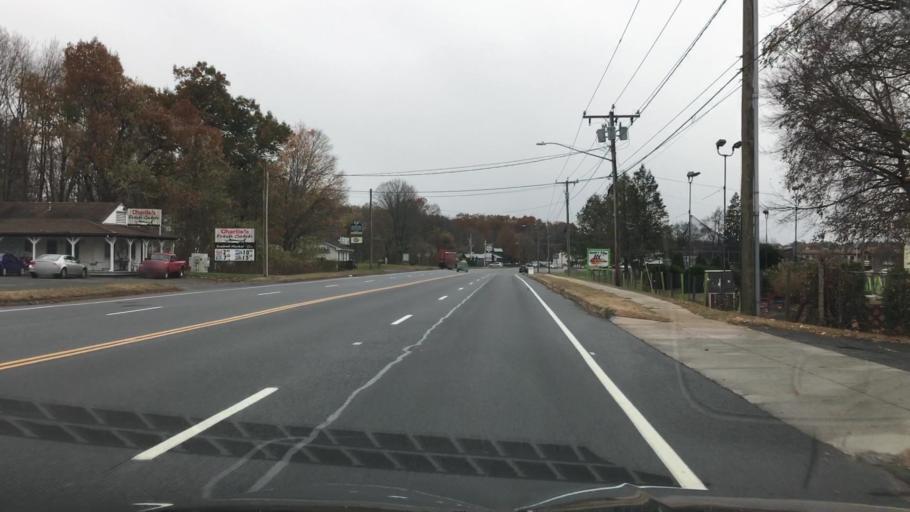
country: US
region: Connecticut
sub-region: Hartford County
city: Manchester
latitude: 41.8192
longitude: -72.5021
